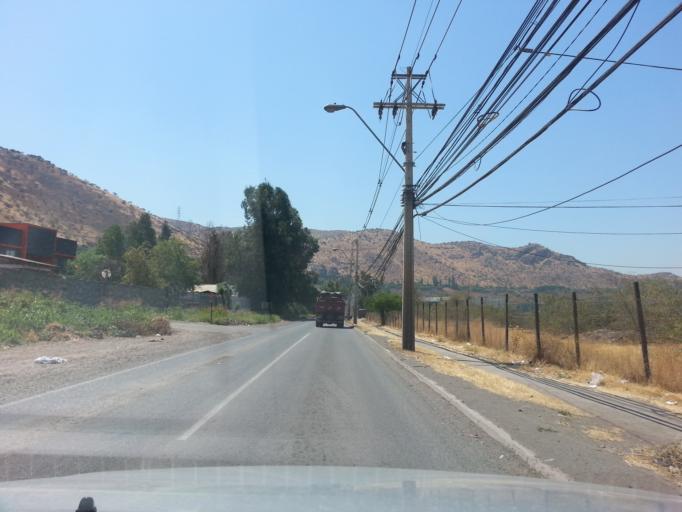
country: CL
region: Santiago Metropolitan
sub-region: Provincia de Chacabuco
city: Chicureo Abajo
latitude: -33.3294
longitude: -70.7006
